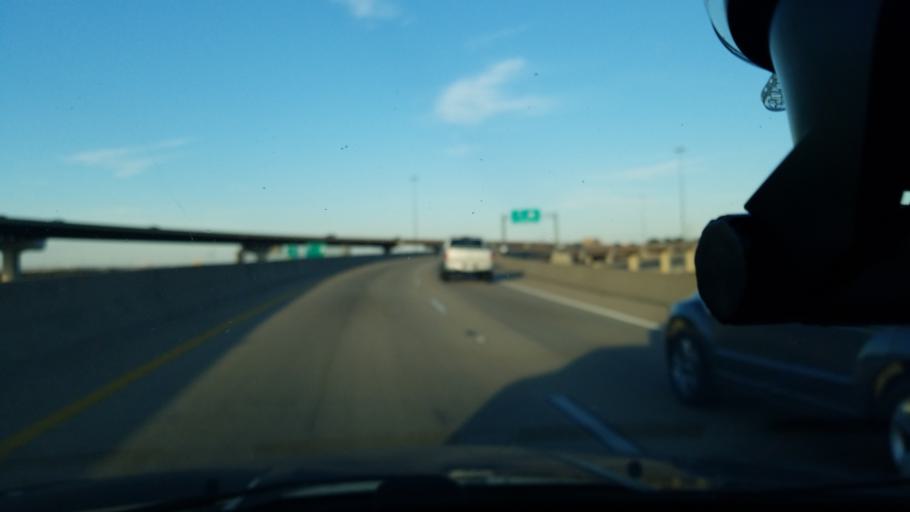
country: US
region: Texas
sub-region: Travis County
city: Wells Branch
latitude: 30.4753
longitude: -97.7016
